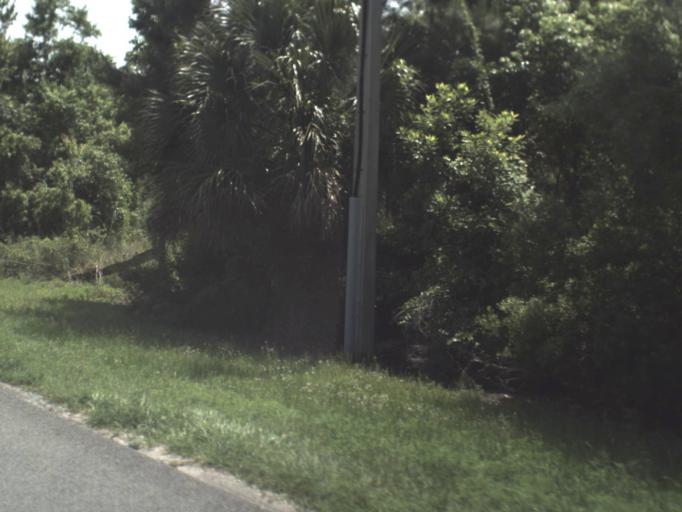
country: US
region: Florida
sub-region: Nassau County
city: Yulee
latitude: 30.5022
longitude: -81.6230
